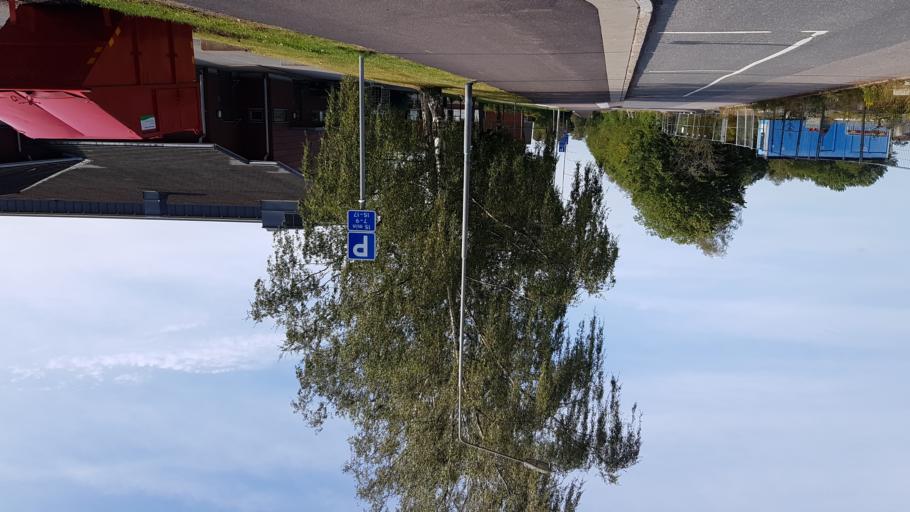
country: SE
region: Vaestra Goetaland
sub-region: Molndal
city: Moelndal
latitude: 57.6650
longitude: 12.0364
